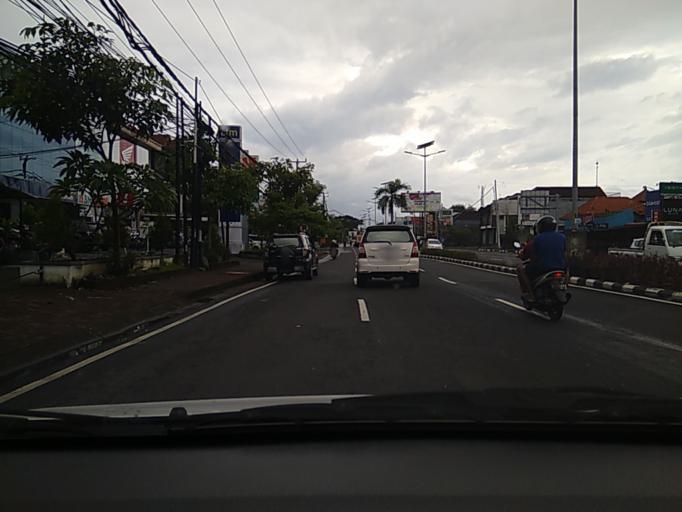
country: ID
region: Bali
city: Bualu
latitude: -8.7901
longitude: 115.2120
